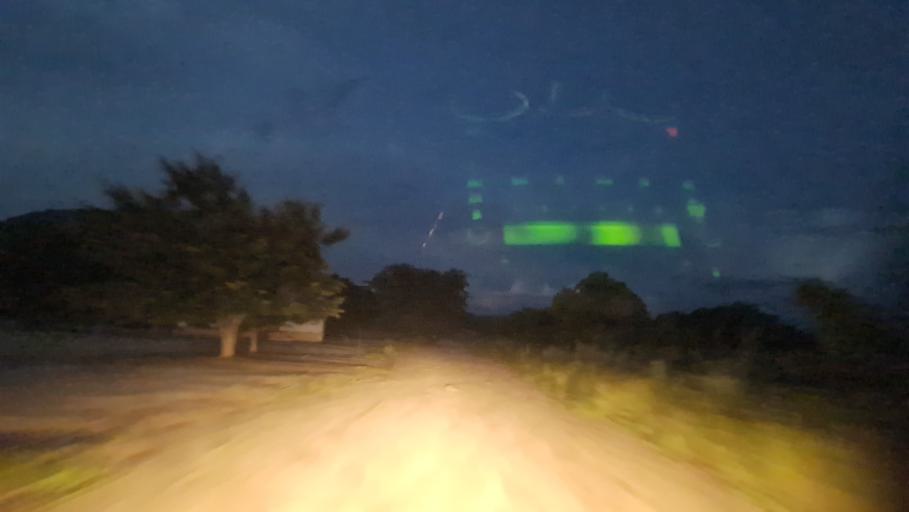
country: MZ
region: Nampula
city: Nampula
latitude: -14.6640
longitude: 39.8373
